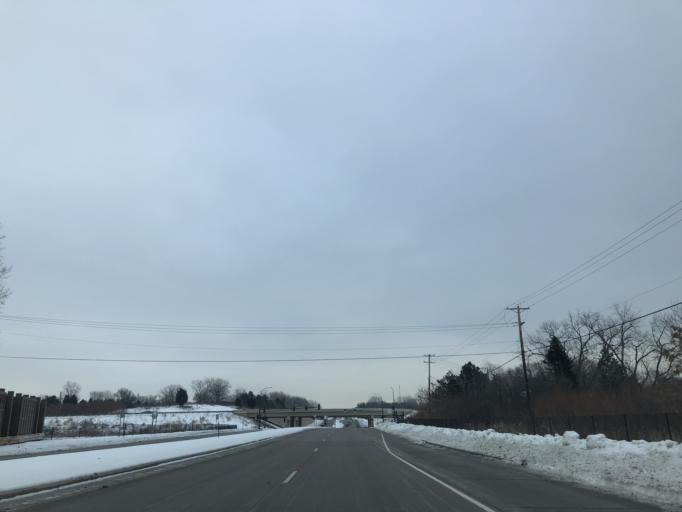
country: US
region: Minnesota
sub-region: Ramsey County
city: New Brighton
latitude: 45.0792
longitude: -93.1797
